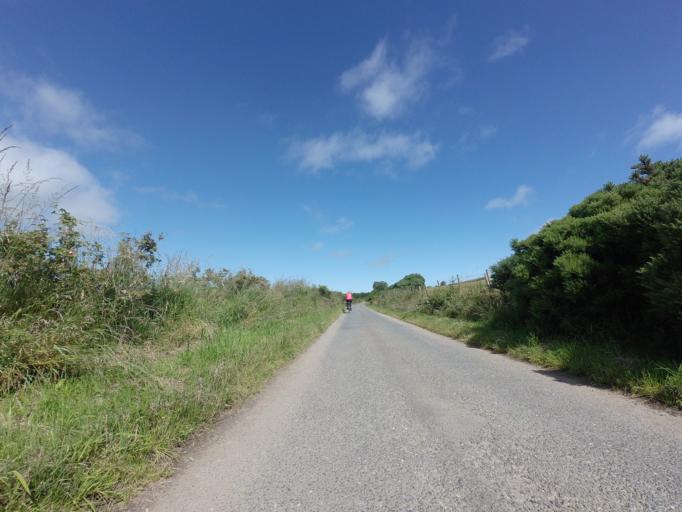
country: GB
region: Scotland
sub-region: Aberdeenshire
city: Banff
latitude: 57.6023
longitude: -2.5123
